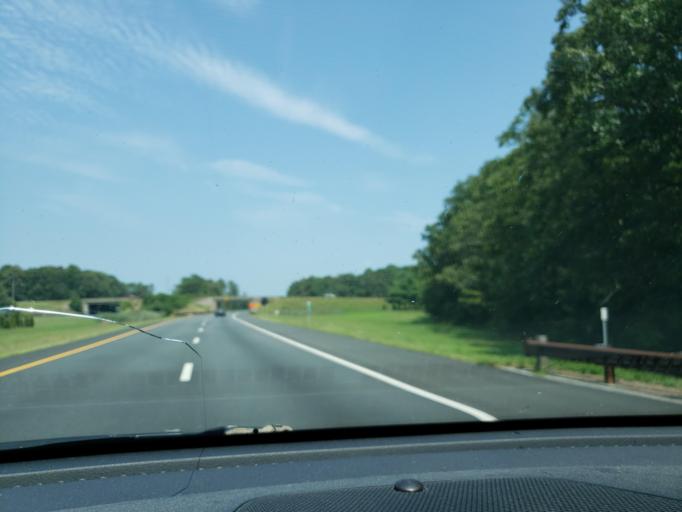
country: US
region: New Jersey
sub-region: Atlantic County
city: Somers Point
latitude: 39.3220
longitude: -74.6185
